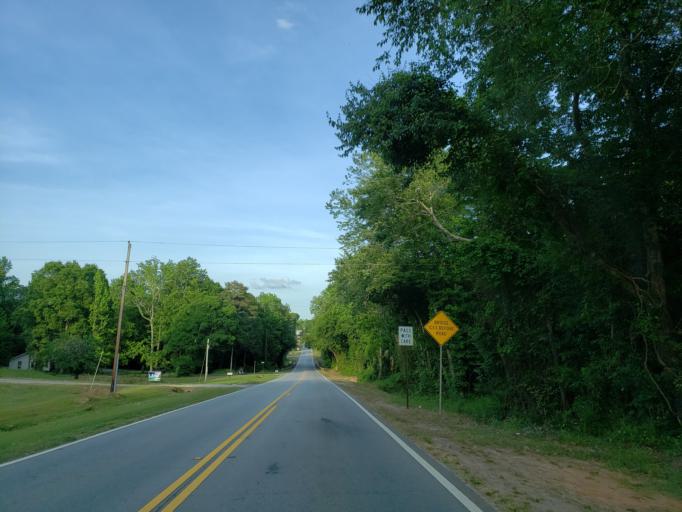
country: US
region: Georgia
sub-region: Carroll County
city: Carrollton
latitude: 33.5884
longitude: -85.1087
